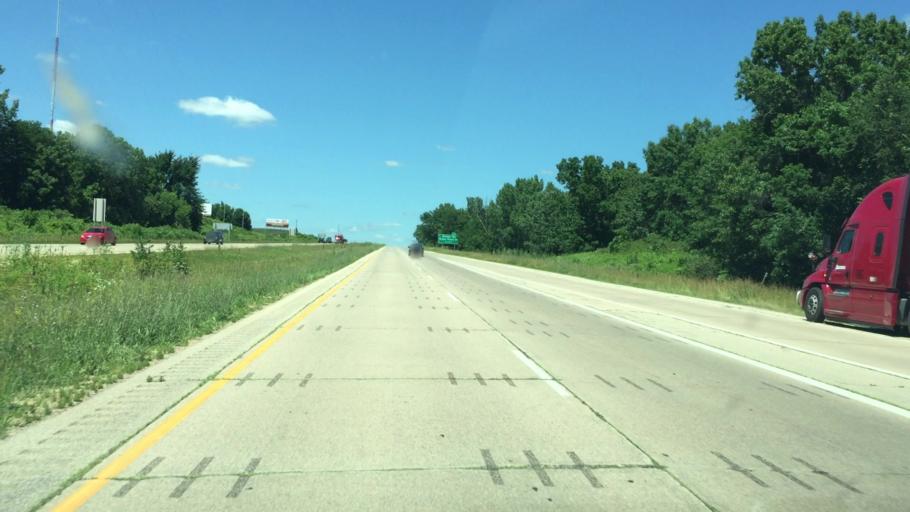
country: US
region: Illinois
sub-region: Jo Daviess County
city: East Dubuque
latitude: 42.5228
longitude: -90.6143
